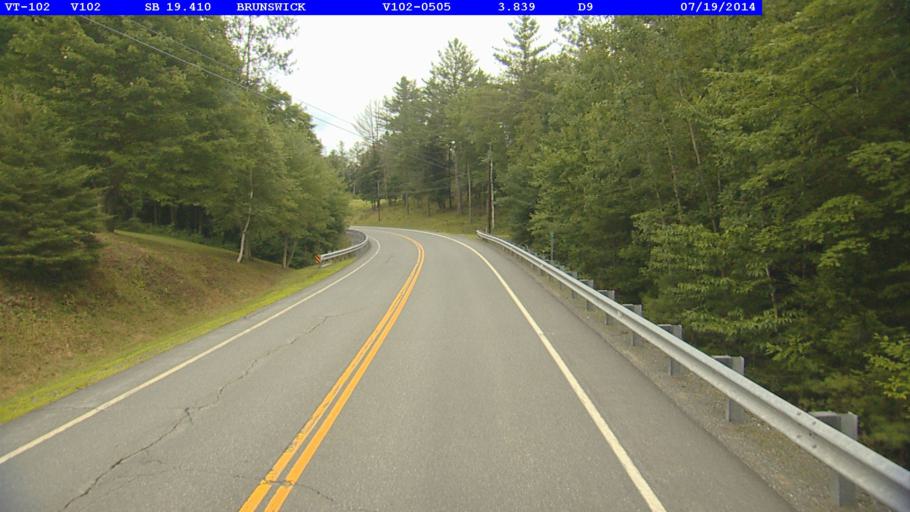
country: US
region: New Hampshire
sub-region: Coos County
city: Stratford
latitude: 44.7126
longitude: -71.6107
